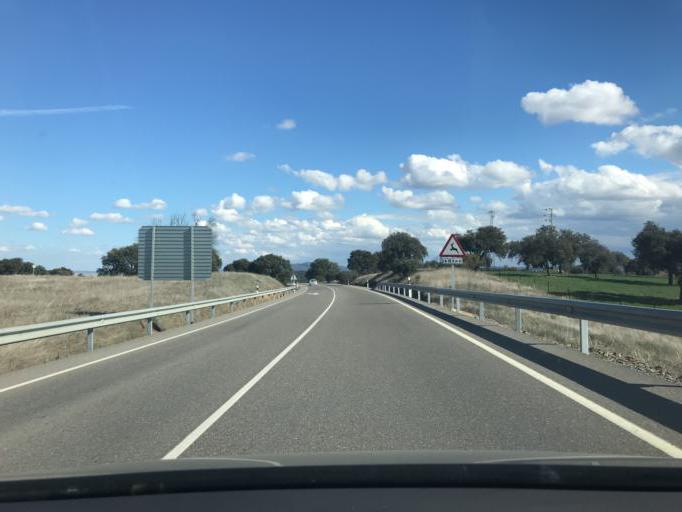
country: ES
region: Andalusia
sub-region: Province of Cordoba
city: Fuente Obejuna
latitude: 38.2591
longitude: -5.4739
